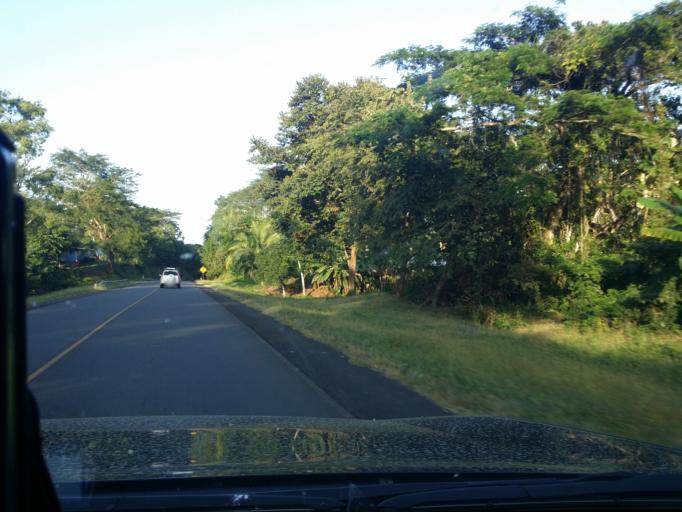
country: NI
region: Rio San Juan
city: San Miguelito
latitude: 11.4897
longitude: -84.8428
